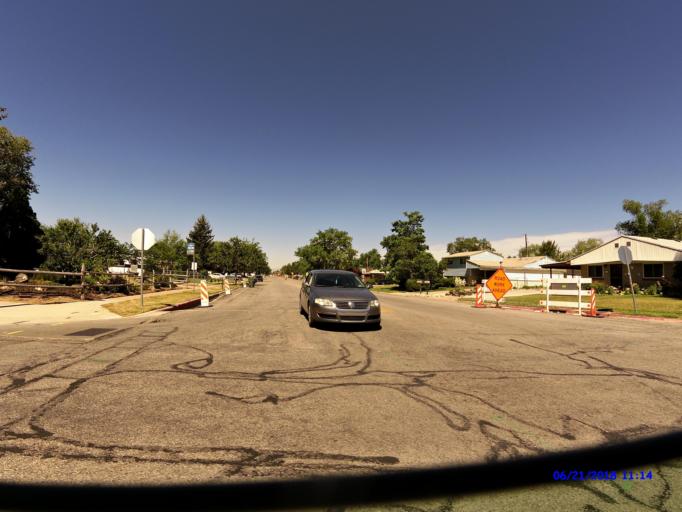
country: US
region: Utah
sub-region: Weber County
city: Harrisville
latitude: 41.2772
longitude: -111.9589
